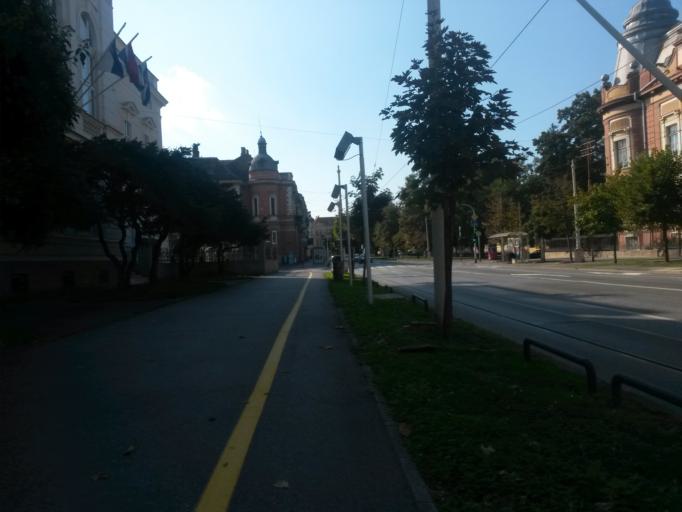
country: HR
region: Osjecko-Baranjska
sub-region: Grad Osijek
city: Osijek
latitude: 45.5607
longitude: 18.6832
